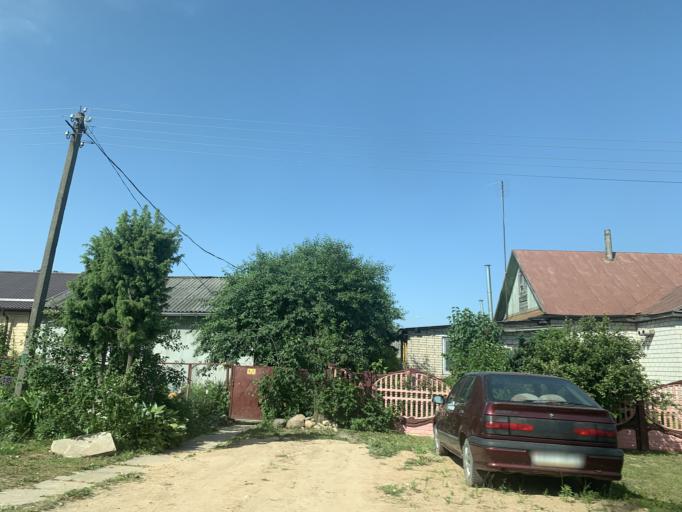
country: BY
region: Minsk
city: Dzyarzhynsk
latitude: 53.7015
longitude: 27.0958
